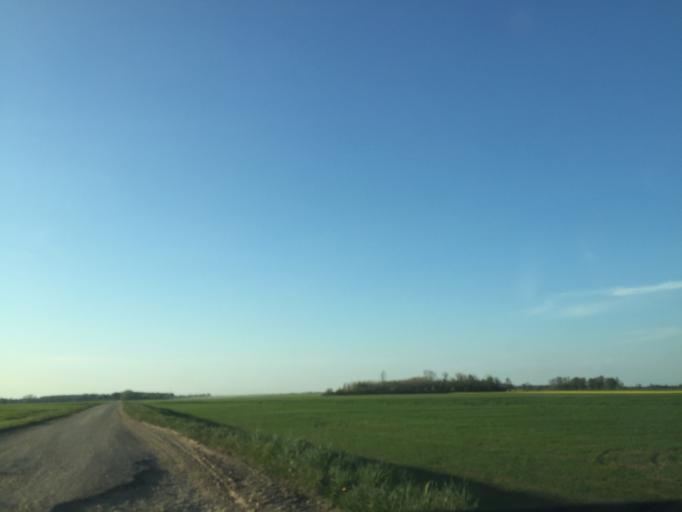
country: LV
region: Bauskas Rajons
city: Bauska
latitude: 56.2815
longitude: 24.2655
